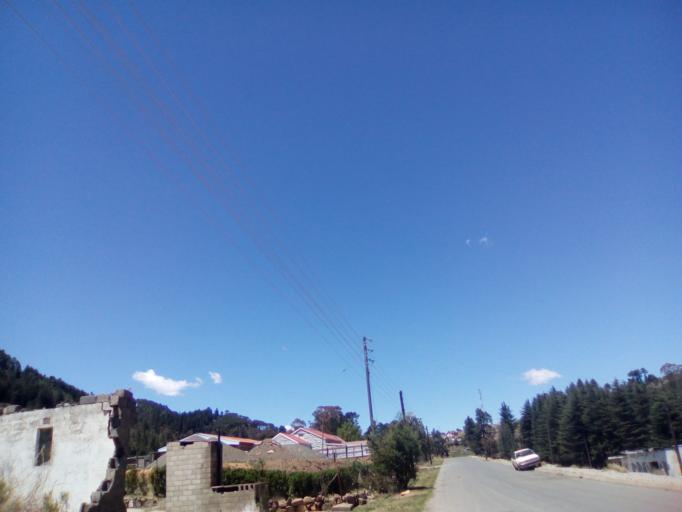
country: LS
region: Qacha's Nek
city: Qacha's Nek
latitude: -30.1187
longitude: 28.6915
